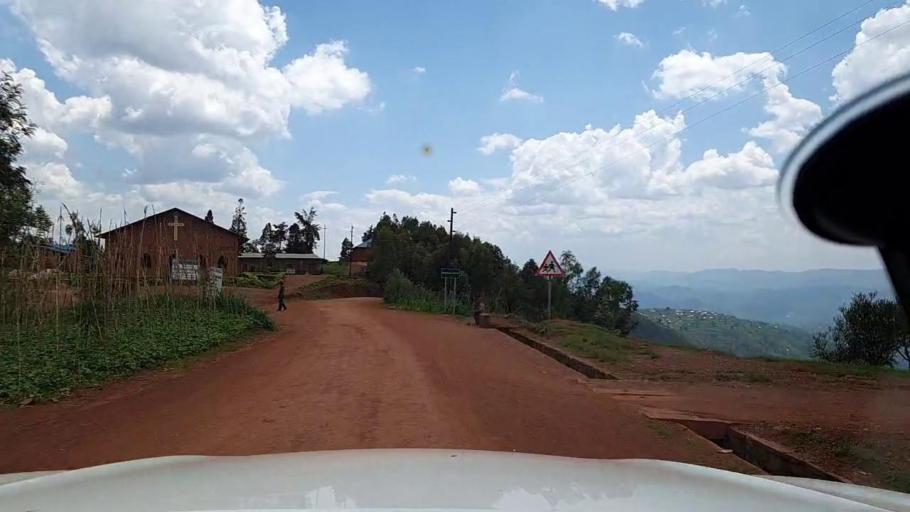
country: RW
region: Kigali
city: Kigali
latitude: -1.7977
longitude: 29.8441
